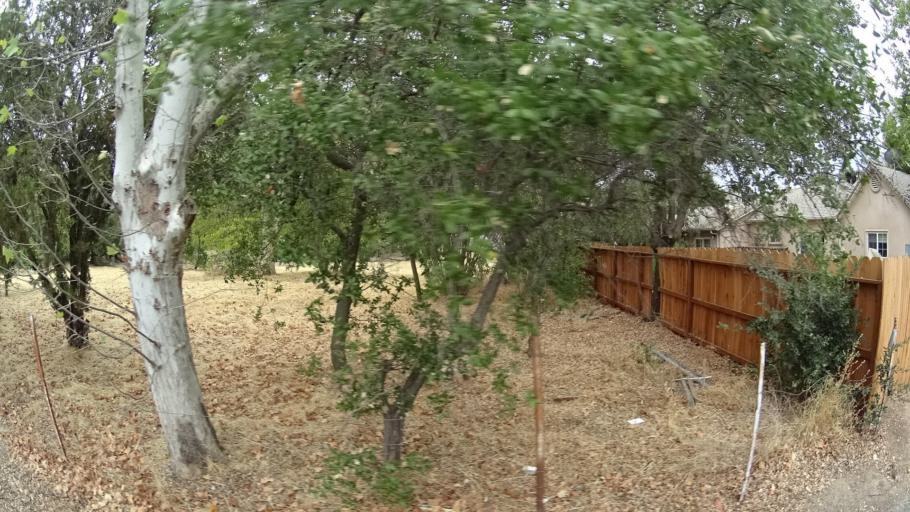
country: US
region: California
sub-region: Placer County
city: Rocklin
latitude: 38.7867
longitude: -121.2381
